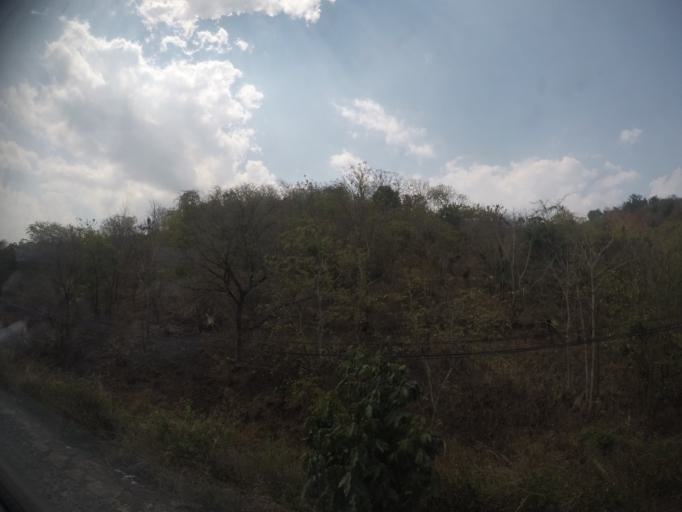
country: VN
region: Binh Thuan
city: Thuan Nam
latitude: 10.8750
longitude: 107.7158
